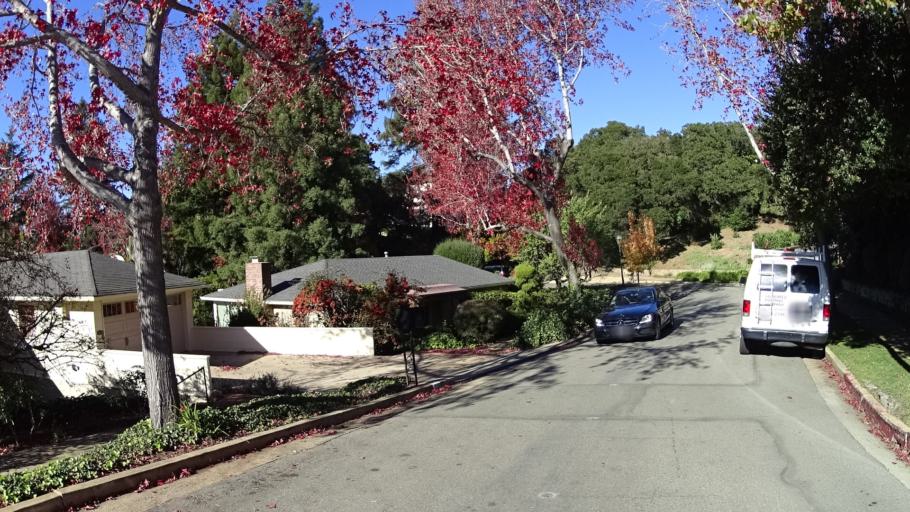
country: US
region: California
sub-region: Alameda County
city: Piedmont
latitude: 37.8160
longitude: -122.2150
